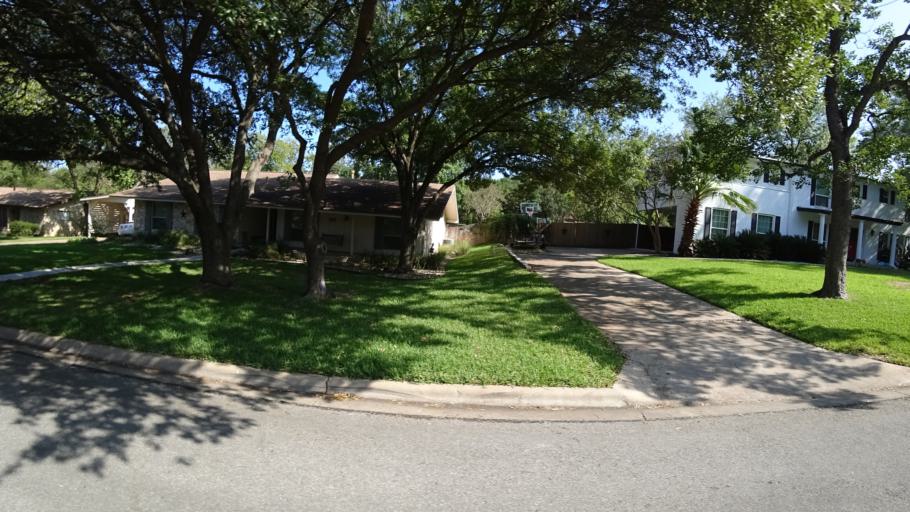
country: US
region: Texas
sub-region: Travis County
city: Rollingwood
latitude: 30.2806
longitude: -97.7981
